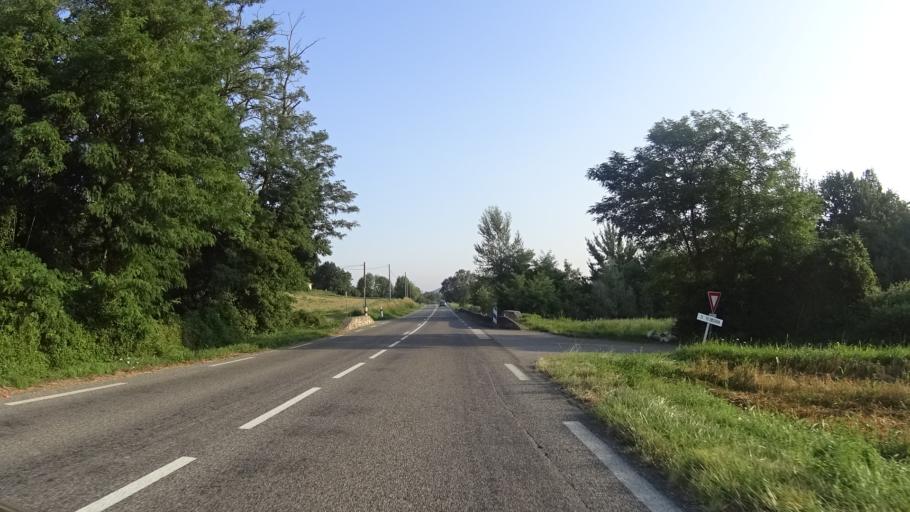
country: FR
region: Midi-Pyrenees
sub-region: Departement de l'Ariege
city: Mirepoix
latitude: 43.0724
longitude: 1.8789
